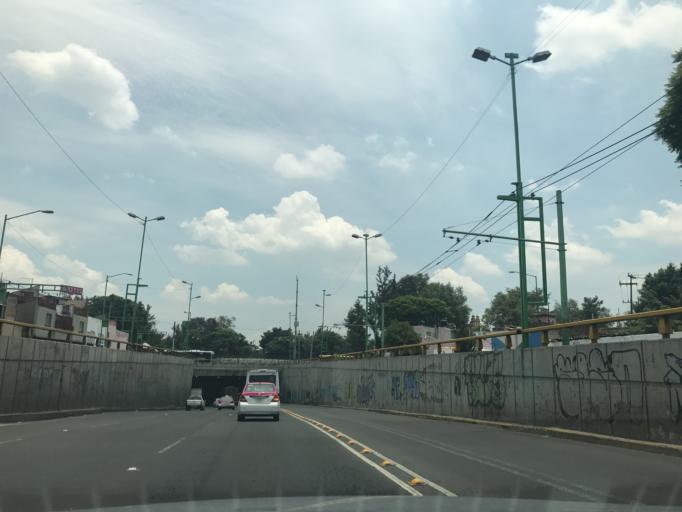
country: MX
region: Mexico City
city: Cuauhtemoc
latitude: 19.4677
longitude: -99.1368
